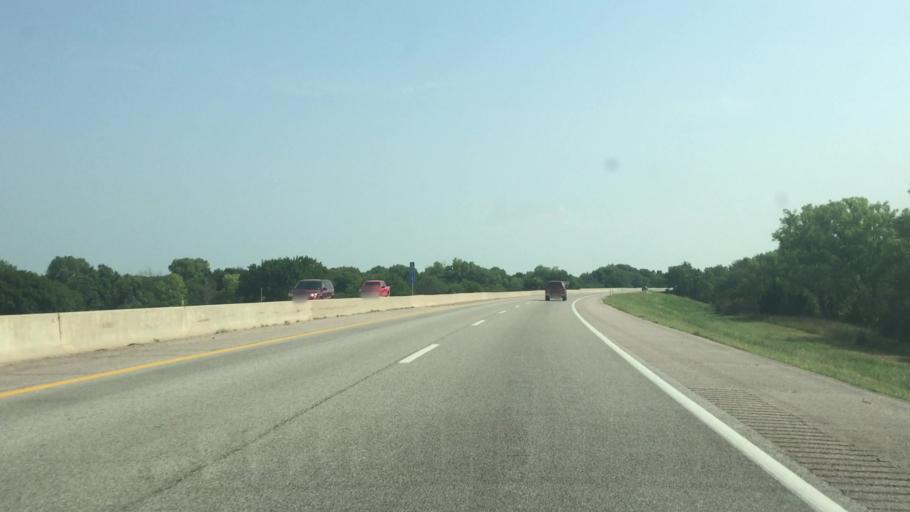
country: US
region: Kansas
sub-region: Butler County
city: El Dorado
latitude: 37.8667
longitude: -96.8575
